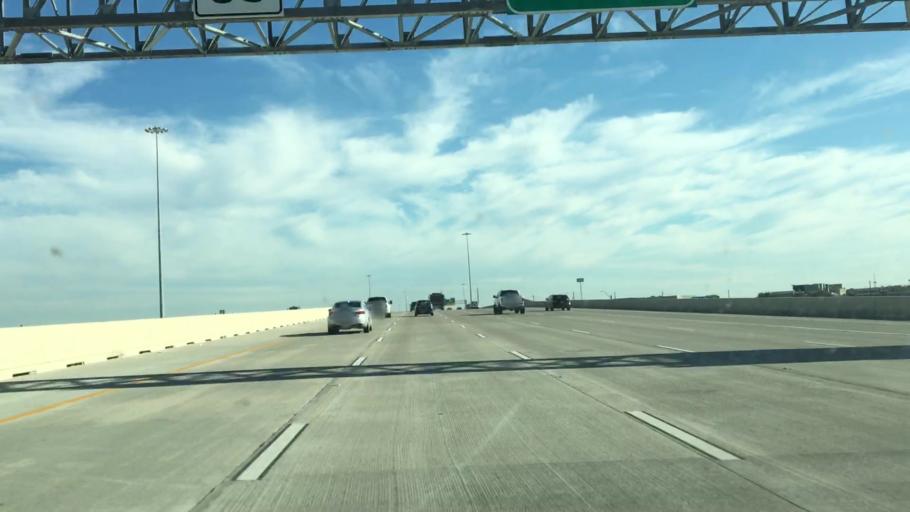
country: US
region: Texas
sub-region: Harris County
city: Webster
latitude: 29.5425
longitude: -95.1436
